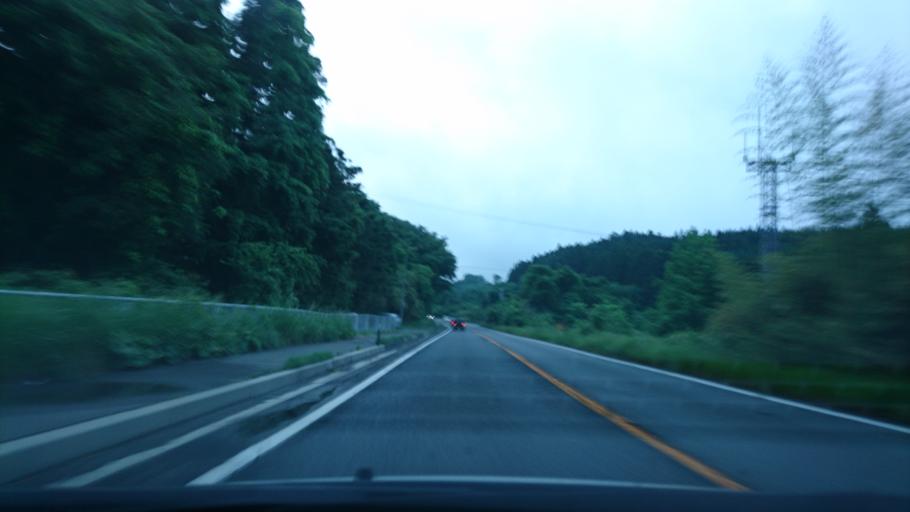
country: JP
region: Iwate
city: Ichinoseki
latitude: 38.9008
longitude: 141.1132
